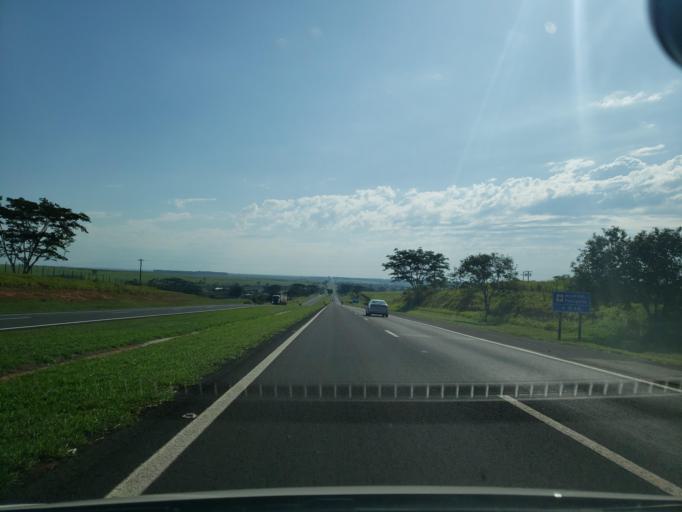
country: BR
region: Sao Paulo
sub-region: Penapolis
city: Penapolis
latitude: -21.5066
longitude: -50.0252
